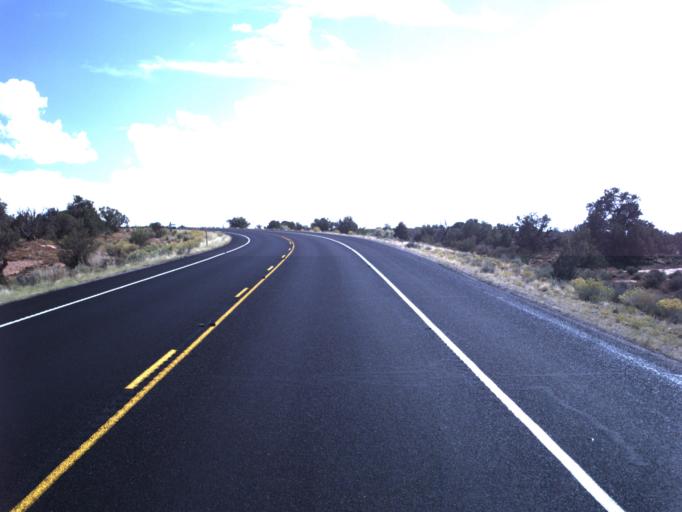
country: US
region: Utah
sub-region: Grand County
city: Moab
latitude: 38.6063
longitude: -109.8173
